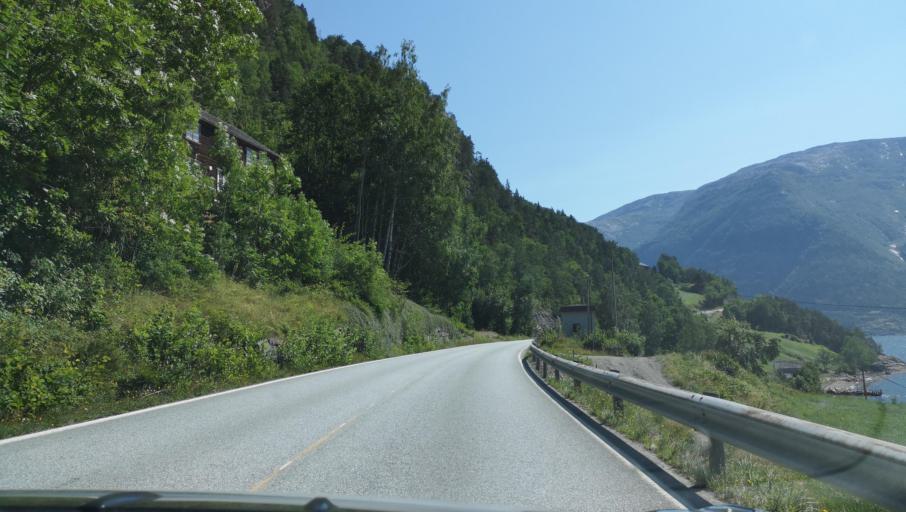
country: NO
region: Hordaland
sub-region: Ulvik
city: Ulvik
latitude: 60.4902
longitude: 6.8662
